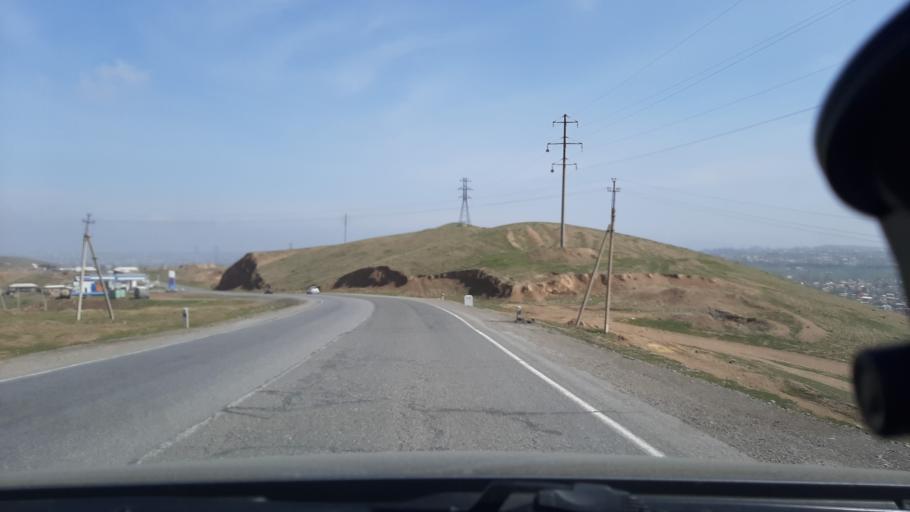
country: TJ
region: Viloyati Sughd
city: Istaravshan
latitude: 39.8523
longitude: 68.9856
